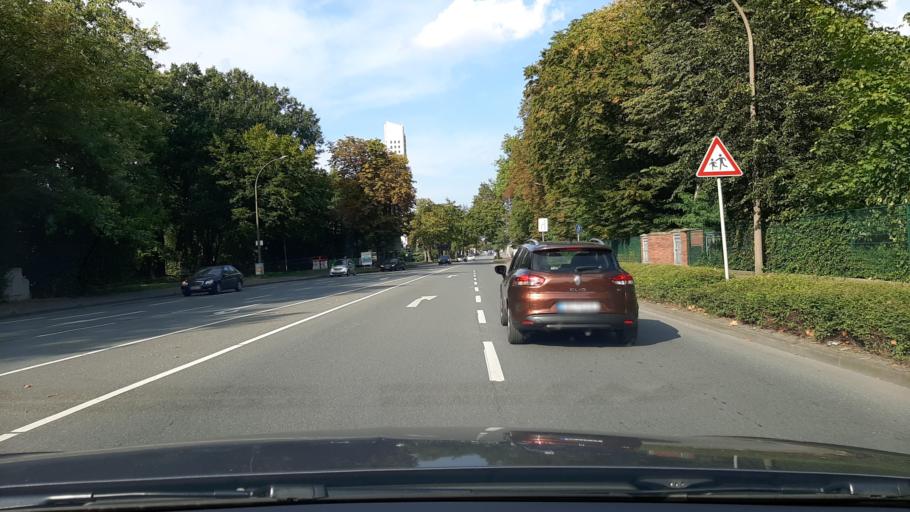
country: DE
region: North Rhine-Westphalia
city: Ahlen
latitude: 51.7716
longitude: 7.8958
